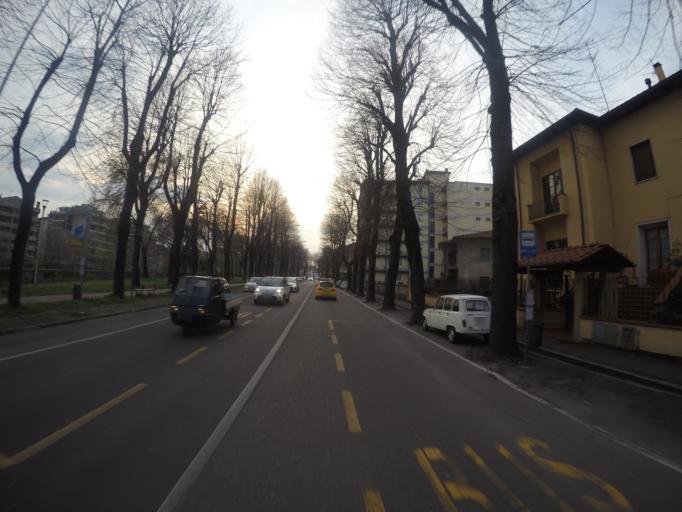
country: IT
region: Tuscany
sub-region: Provincia di Prato
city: Prato
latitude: 43.8736
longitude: 11.1134
